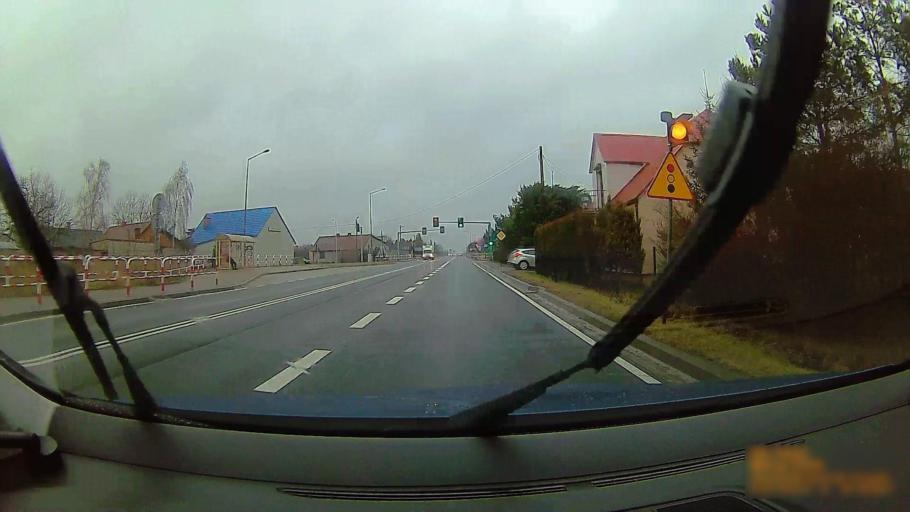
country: PL
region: Greater Poland Voivodeship
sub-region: Konin
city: Konin
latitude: 52.1755
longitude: 18.2719
